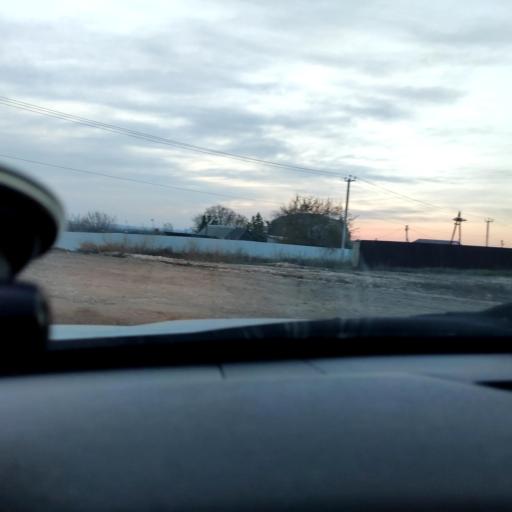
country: RU
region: Samara
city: Smyshlyayevka
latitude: 53.1545
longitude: 50.3928
